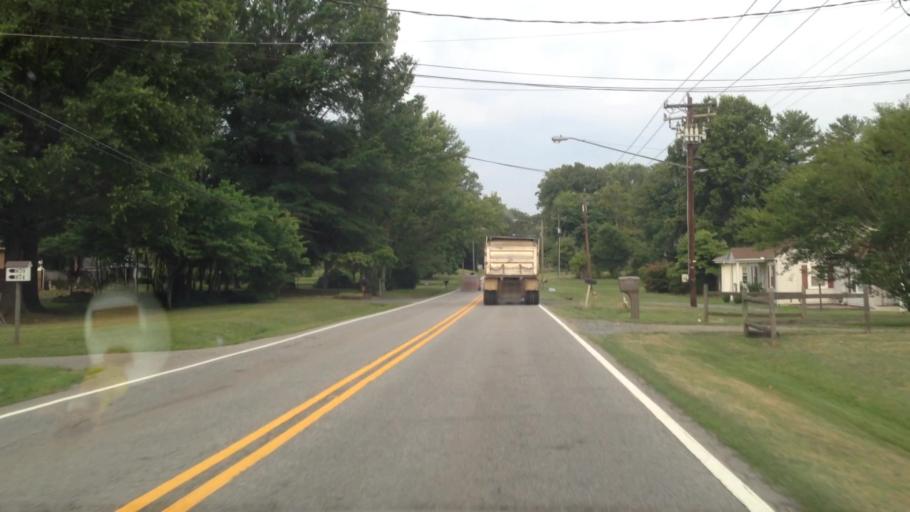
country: US
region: North Carolina
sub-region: Forsyth County
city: Rural Hall
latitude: 36.1917
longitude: -80.2409
